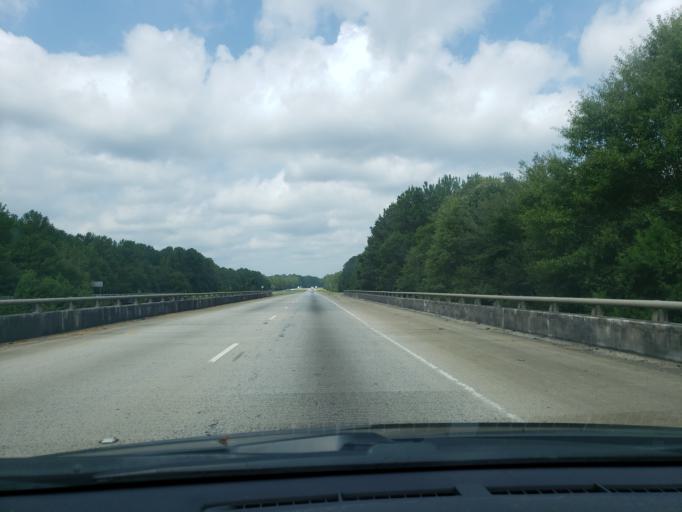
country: US
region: Georgia
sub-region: Emanuel County
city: Swainsboro
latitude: 32.4083
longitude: -82.3358
